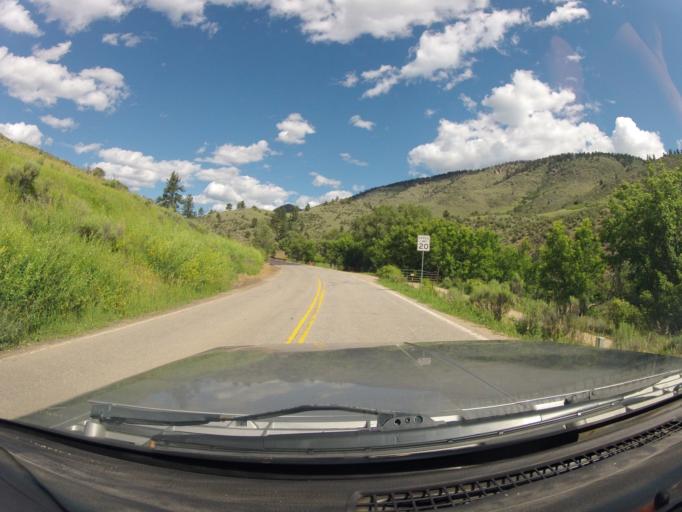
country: US
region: Colorado
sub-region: Larimer County
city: Laporte
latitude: 40.5600
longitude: -105.2956
